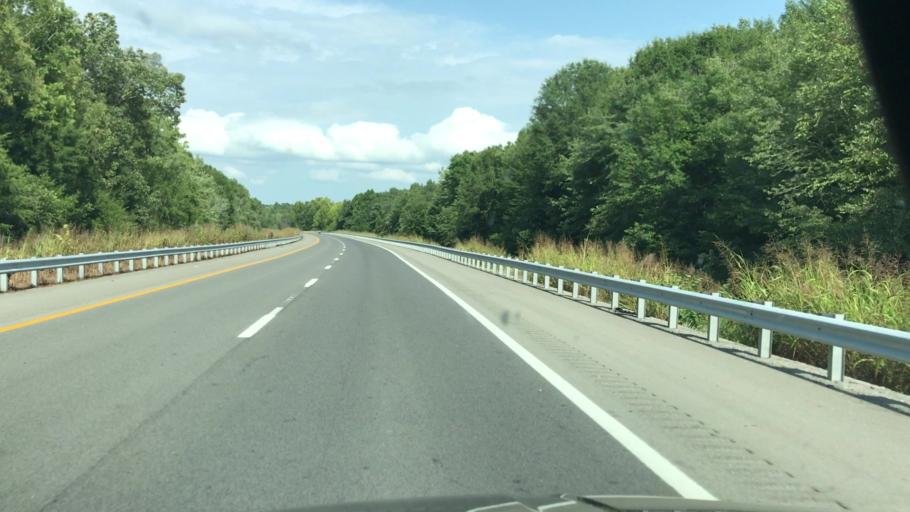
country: US
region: Kentucky
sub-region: Hopkins County
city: Nortonville
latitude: 37.2108
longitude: -87.4108
